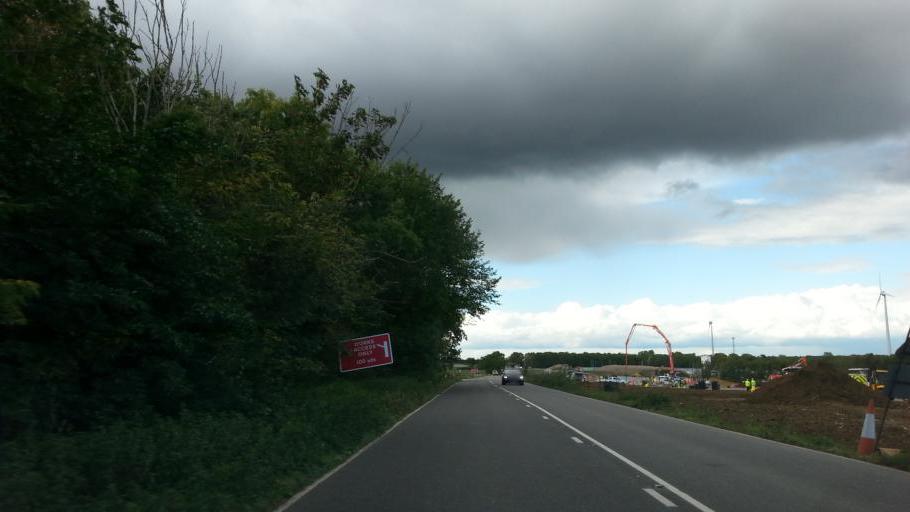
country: GB
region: England
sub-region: Cambridgeshire
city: Godmanchester
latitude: 52.2901
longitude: -0.1480
